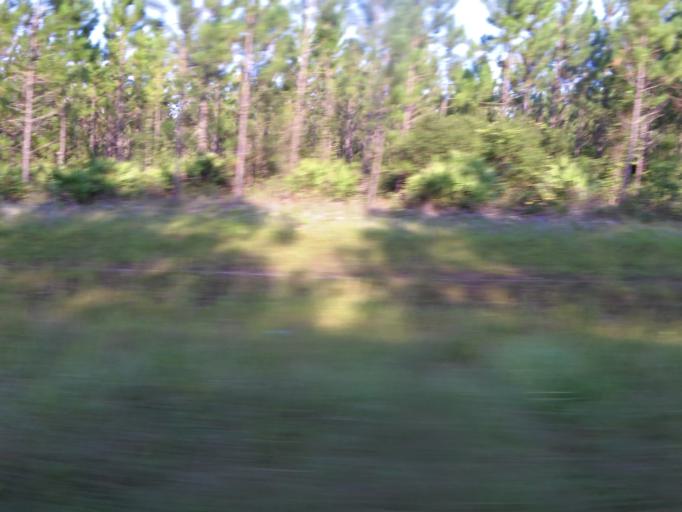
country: US
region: Florida
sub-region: Duval County
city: Baldwin
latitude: 30.3554
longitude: -82.0094
